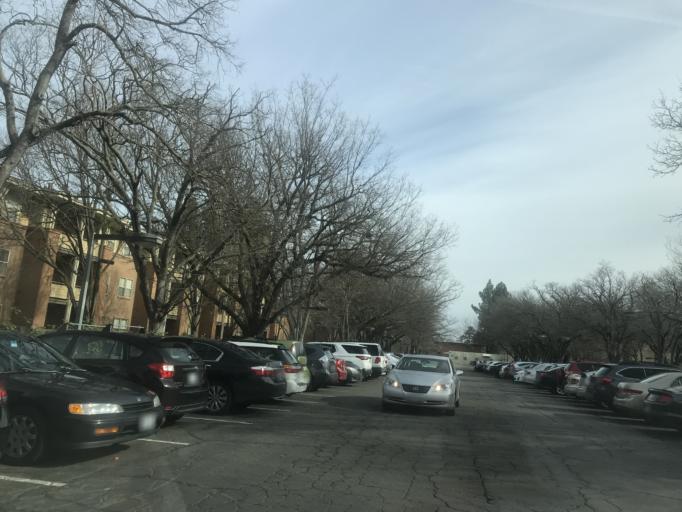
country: US
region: California
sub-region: Yolo County
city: Davis
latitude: 38.5449
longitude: -121.7569
